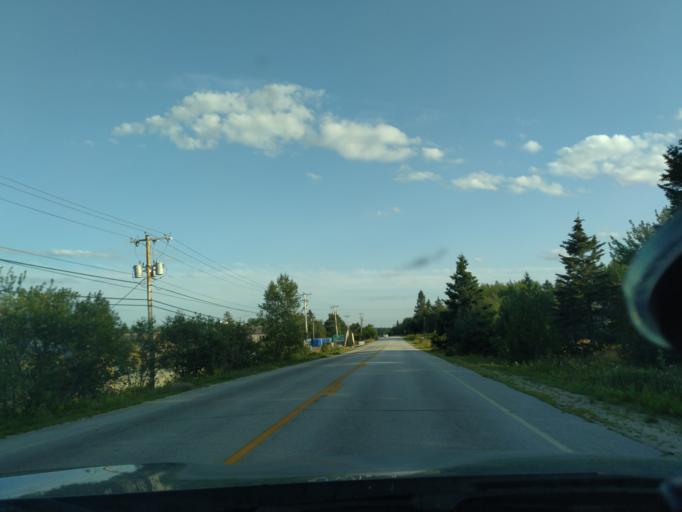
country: US
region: Maine
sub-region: Hancock County
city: Gouldsboro
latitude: 44.4046
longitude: -68.0873
